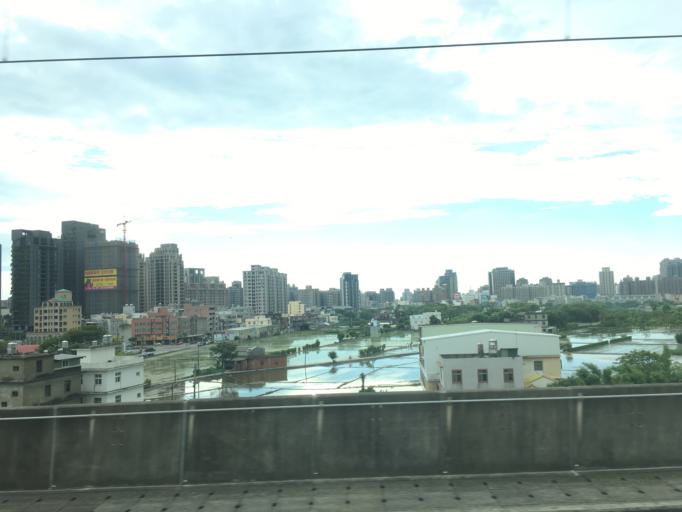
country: TW
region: Taiwan
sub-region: Hsinchu
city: Zhubei
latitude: 24.8137
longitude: 121.0416
